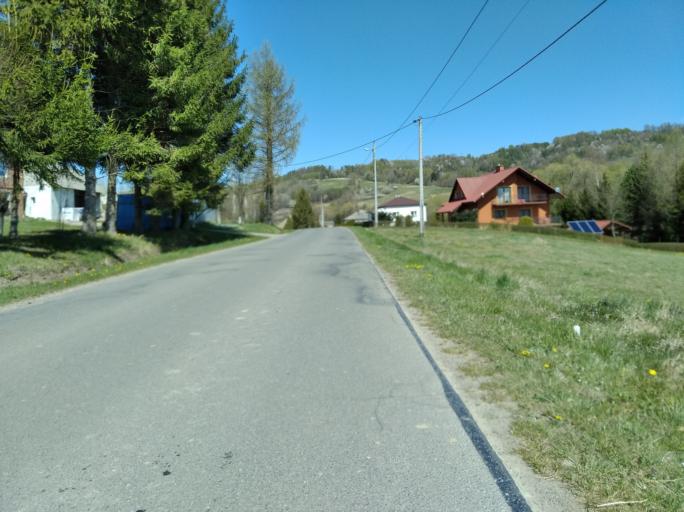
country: PL
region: Subcarpathian Voivodeship
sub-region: Powiat brzozowski
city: Dydnia
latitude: 49.6981
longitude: 22.1520
